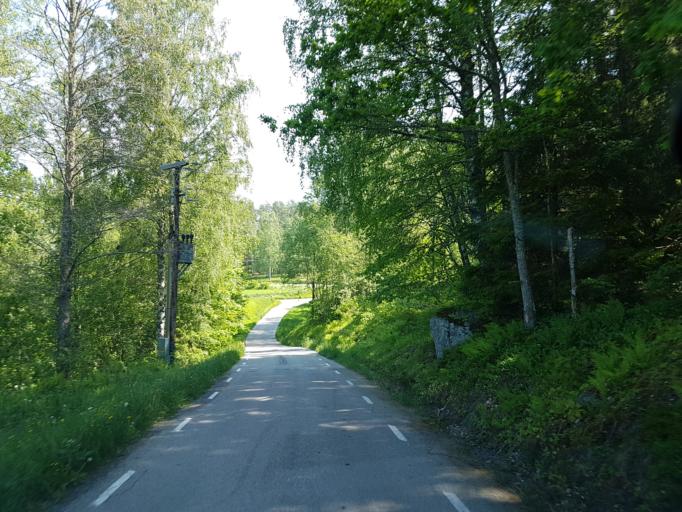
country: SE
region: OEstergoetland
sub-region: Atvidabergs Kommun
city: Atvidaberg
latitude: 58.2382
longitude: 16.1941
